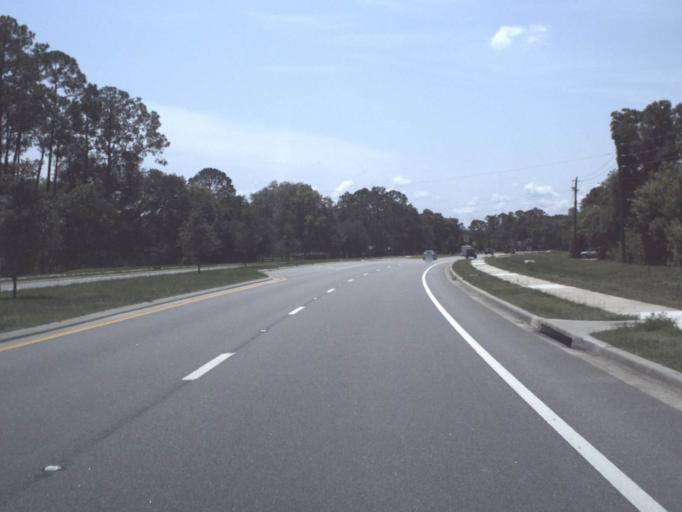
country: US
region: Florida
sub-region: Clay County
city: Green Cove Springs
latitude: 29.9691
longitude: -81.5004
